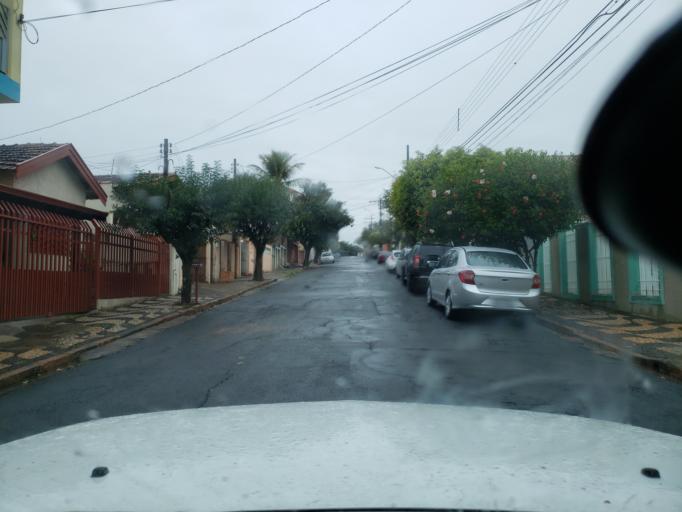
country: BR
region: Sao Paulo
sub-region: Moji-Guacu
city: Mogi-Gaucu
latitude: -22.3780
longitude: -46.9363
